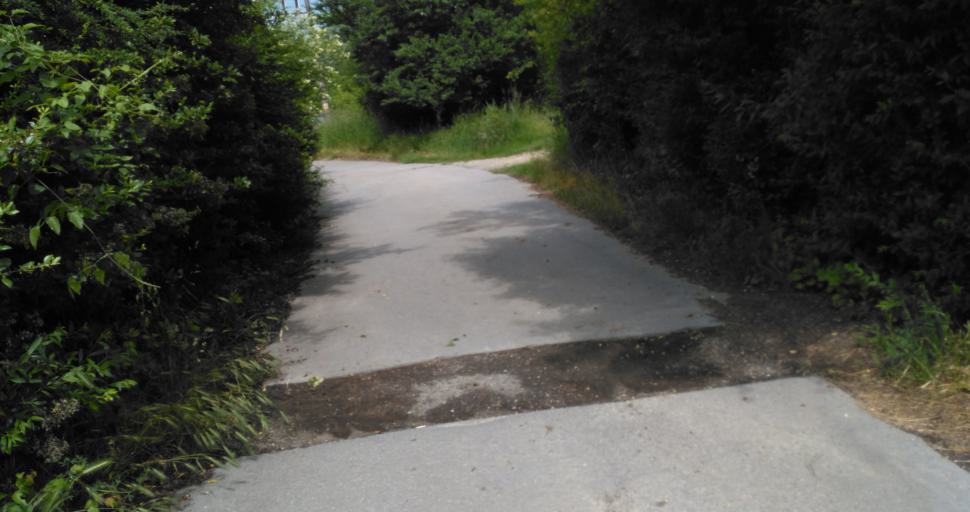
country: CZ
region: South Moravian
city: Podoli
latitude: 49.1893
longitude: 16.6710
